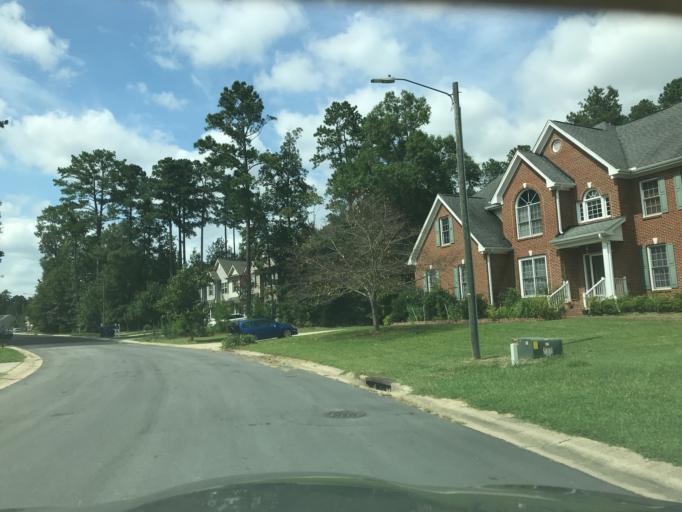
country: US
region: North Carolina
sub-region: Wake County
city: Rolesville
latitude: 35.8930
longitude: -78.5360
